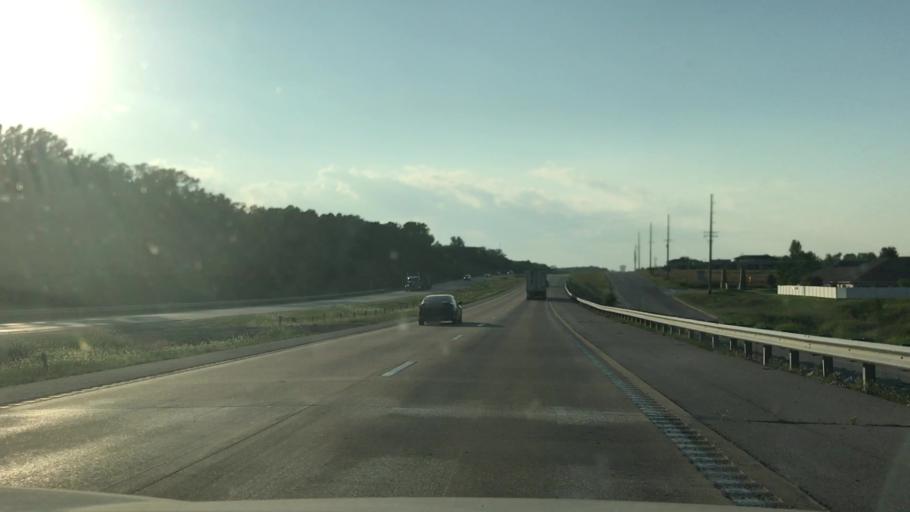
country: US
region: Missouri
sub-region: Saint Charles County
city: Dardenne Prairie
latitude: 38.7270
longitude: -90.7319
